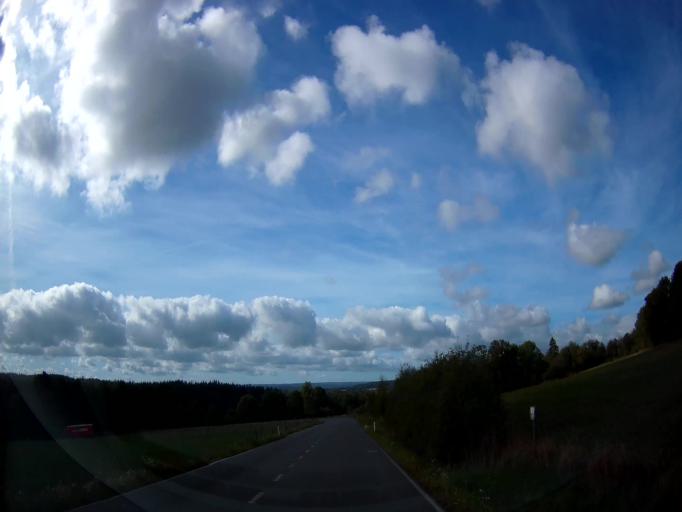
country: BE
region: Wallonia
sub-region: Province du Luxembourg
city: Wellin
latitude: 50.1717
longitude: 5.1262
